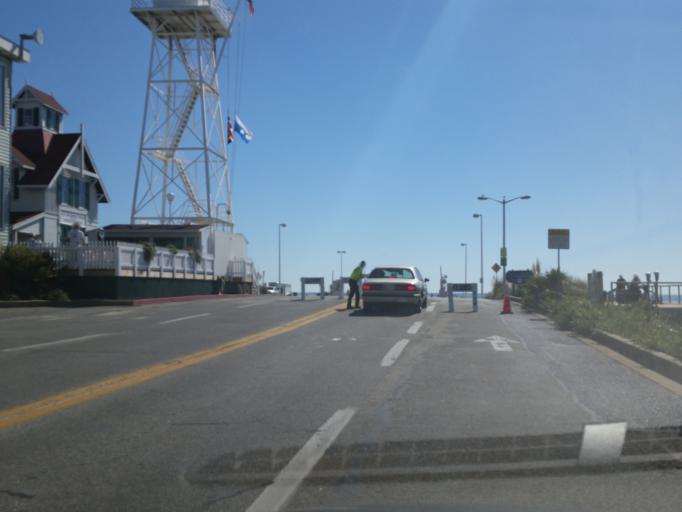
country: US
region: Maryland
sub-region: Worcester County
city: Ocean City
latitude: 38.3254
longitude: -75.0885
